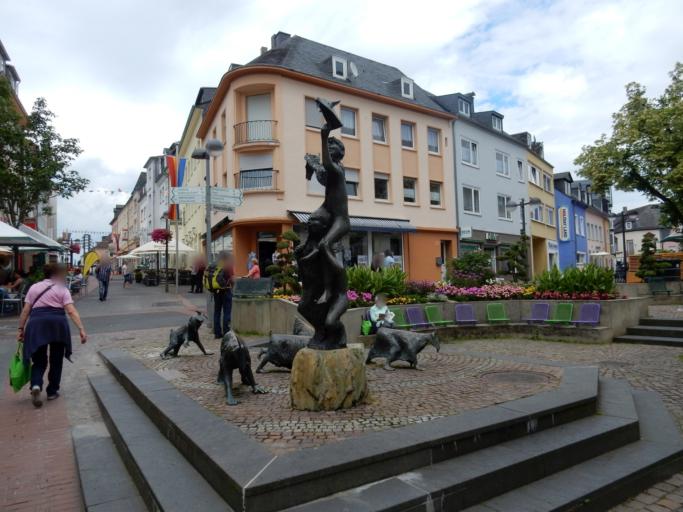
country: DE
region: Rheinland-Pfalz
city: Bitburg
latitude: 49.9736
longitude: 6.5244
